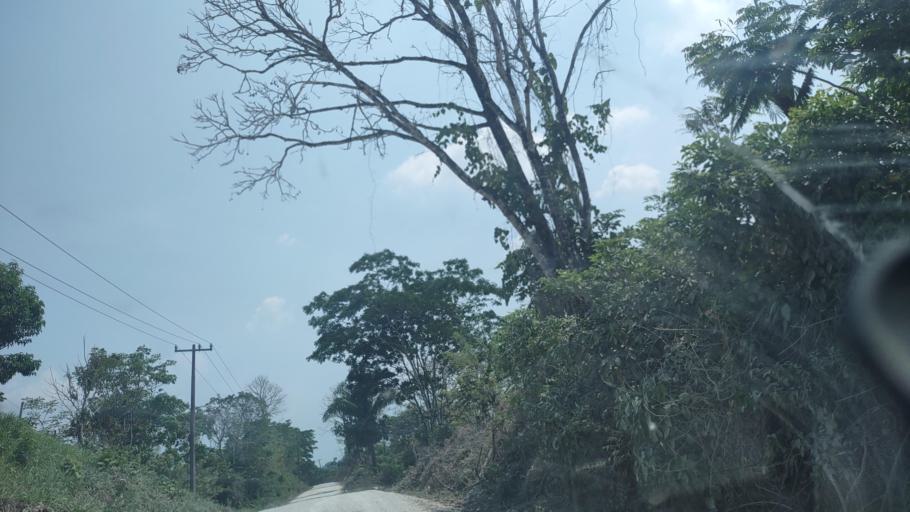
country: MX
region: Tabasco
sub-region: Huimanguillo
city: Francisco Rueda
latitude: 17.5860
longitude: -93.8920
